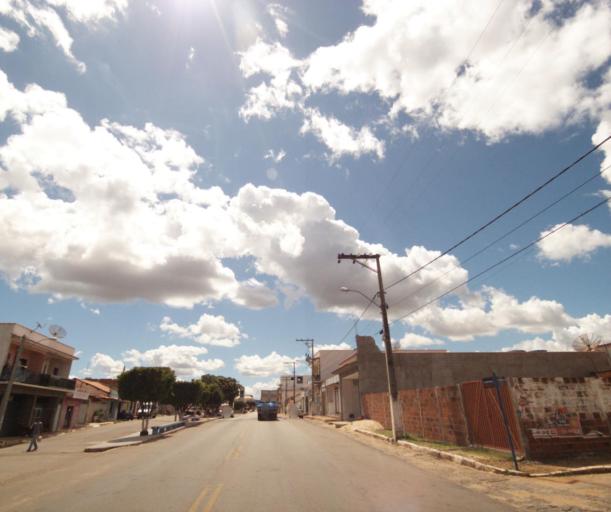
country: BR
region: Bahia
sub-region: Cacule
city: Cacule
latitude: -14.2062
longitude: -42.1104
